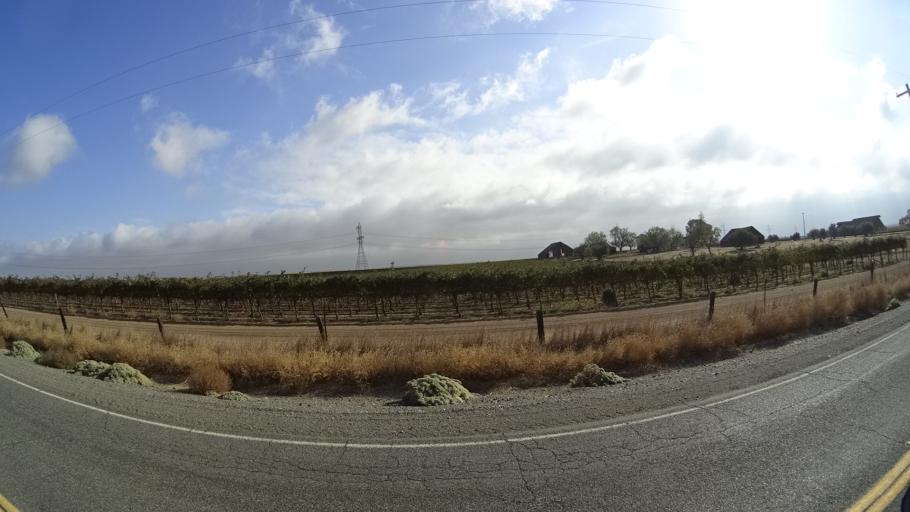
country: US
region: California
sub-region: Yolo County
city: Esparto
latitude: 38.7827
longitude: -122.0077
